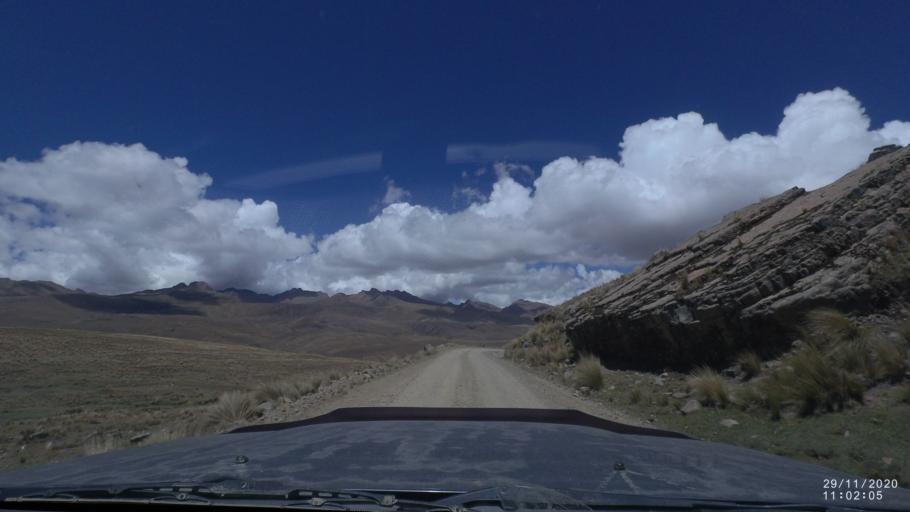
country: BO
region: Cochabamba
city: Cochabamba
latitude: -17.1964
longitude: -66.2251
